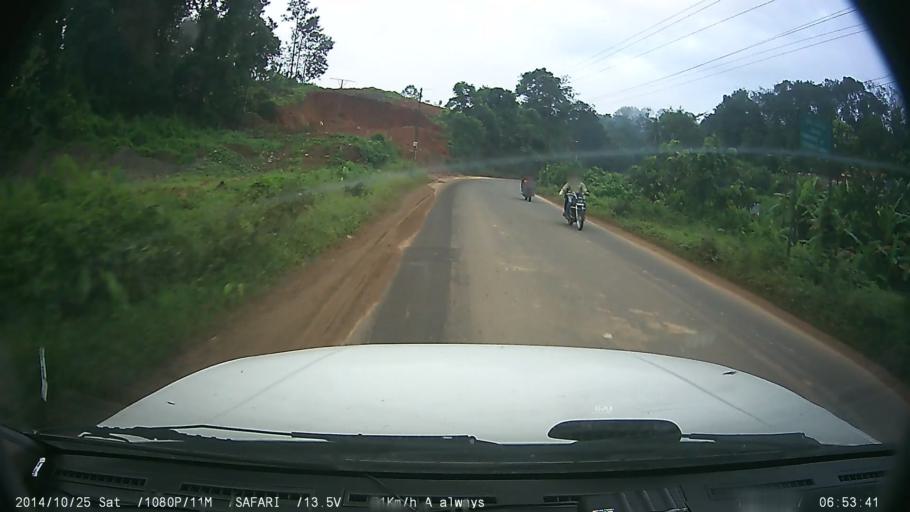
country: IN
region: Kerala
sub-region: Ernakulam
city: Muvattupuzha
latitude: 9.9076
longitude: 76.5840
